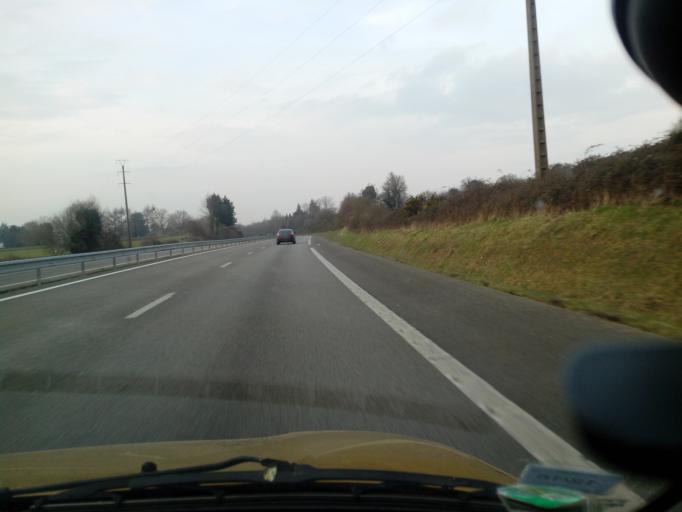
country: FR
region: Brittany
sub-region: Departement du Morbihan
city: Ploermel
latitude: 47.9265
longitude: -2.4148
